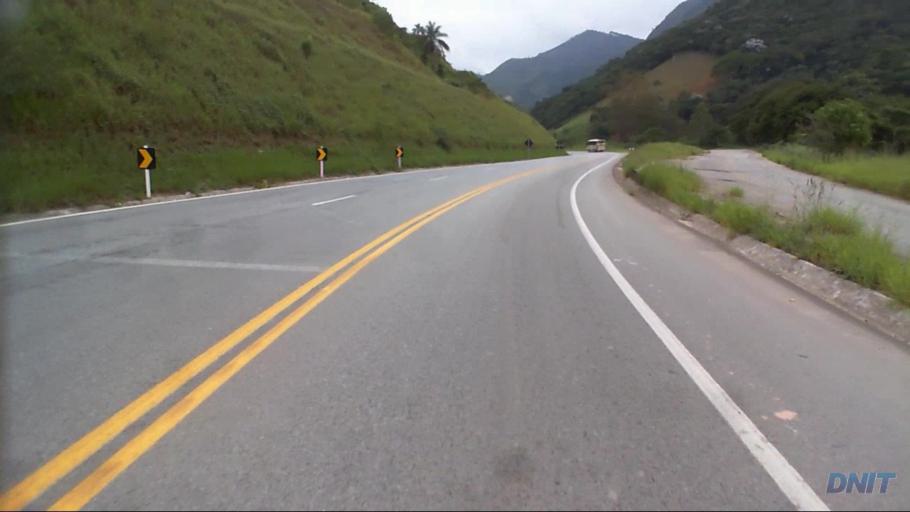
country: BR
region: Minas Gerais
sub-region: Nova Era
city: Nova Era
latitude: -19.6425
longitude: -42.9188
